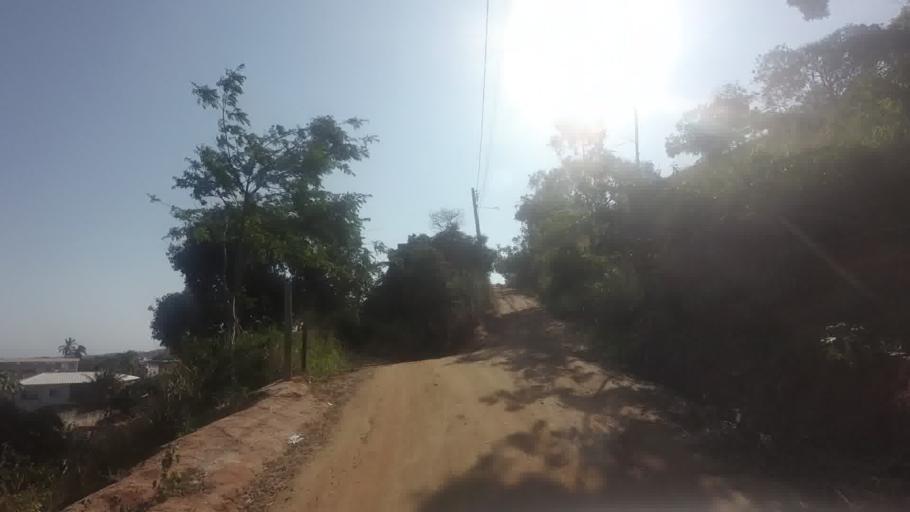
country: BR
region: Espirito Santo
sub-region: Piuma
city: Piuma
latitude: -20.8871
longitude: -40.7738
